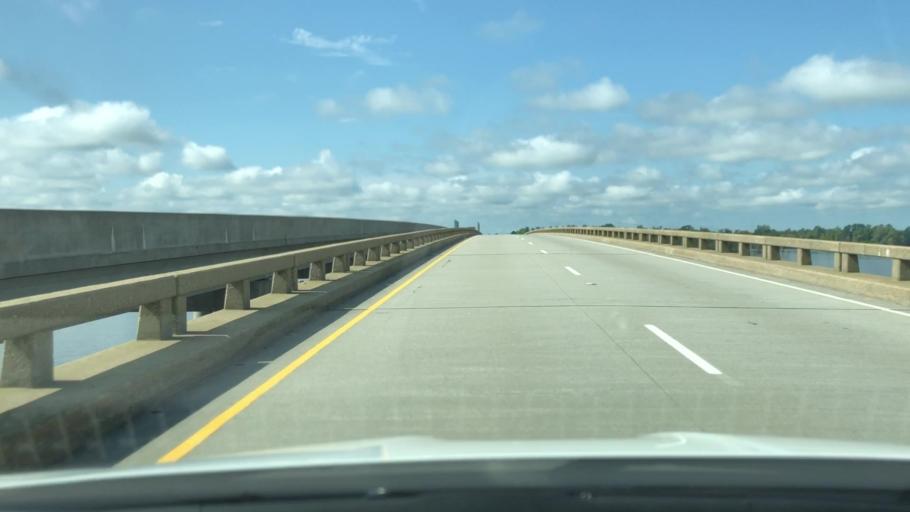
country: US
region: North Carolina
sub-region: Perquimans County
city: Hertford
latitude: 36.1915
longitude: -76.4549
